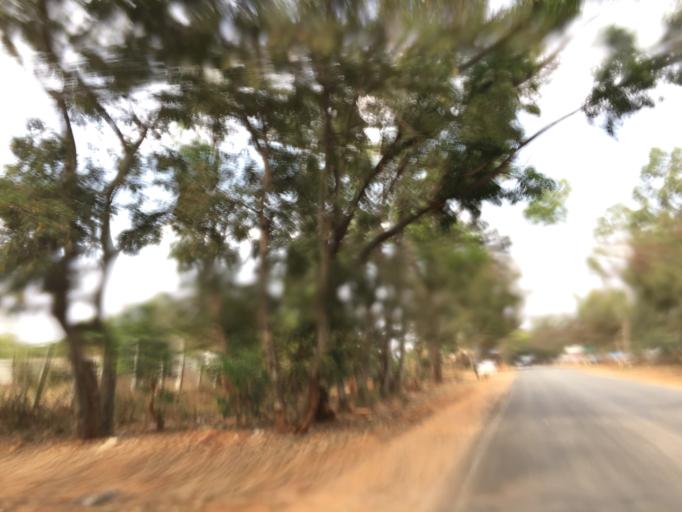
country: IN
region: Karnataka
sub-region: Chikkaballapur
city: Chik Ballapur
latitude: 13.3962
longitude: 77.7037
